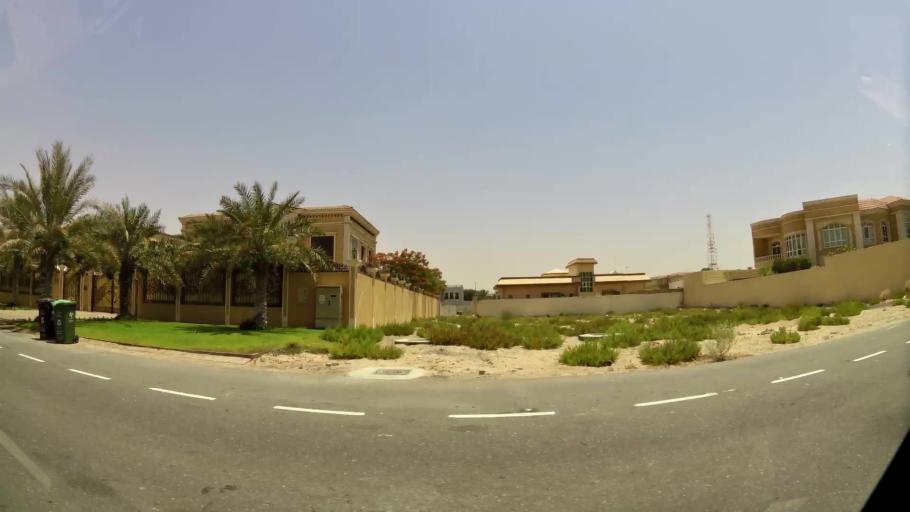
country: AE
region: Dubai
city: Dubai
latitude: 25.0873
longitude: 55.2019
